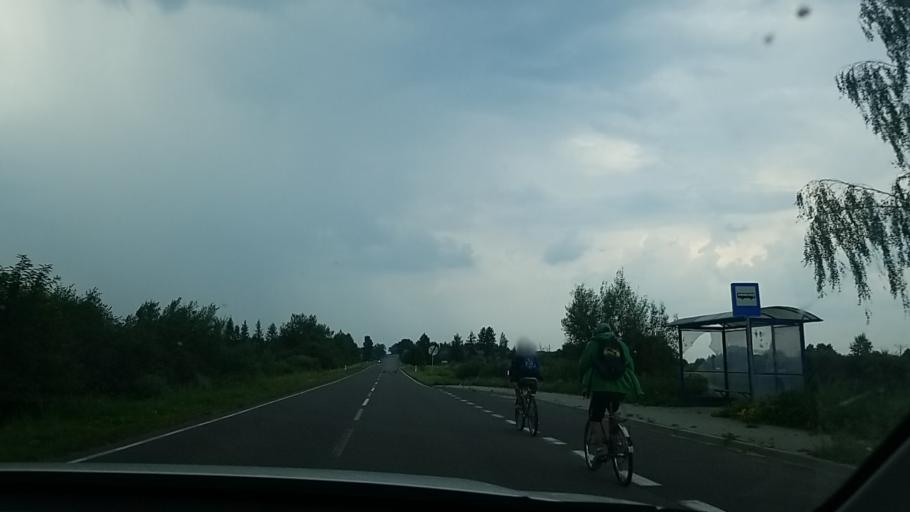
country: PL
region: Lublin Voivodeship
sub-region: Powiat leczynski
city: Cycow
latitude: 51.2549
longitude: 23.0925
